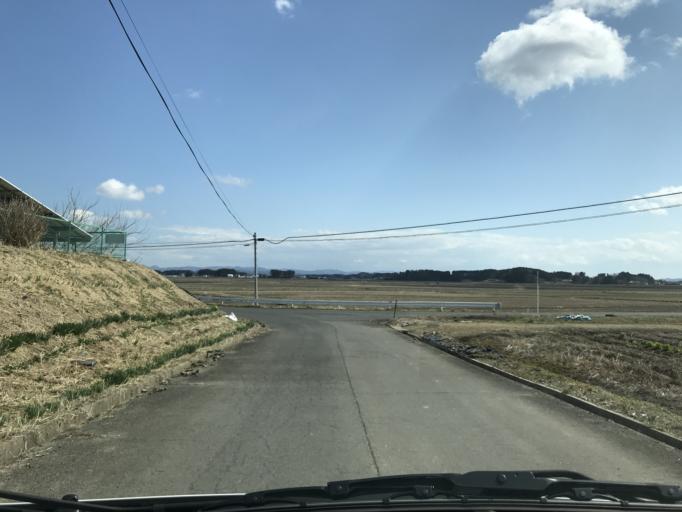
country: JP
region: Miyagi
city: Wakuya
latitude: 38.6848
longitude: 141.1499
